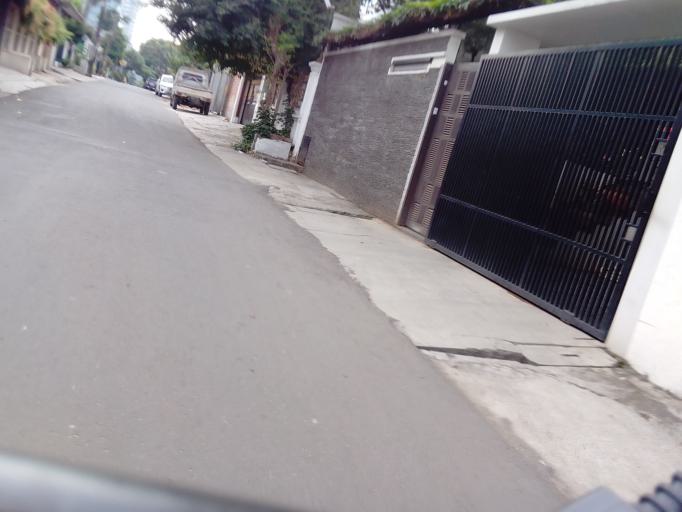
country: ID
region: Jakarta Raya
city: Jakarta
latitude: -6.2055
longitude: 106.8058
